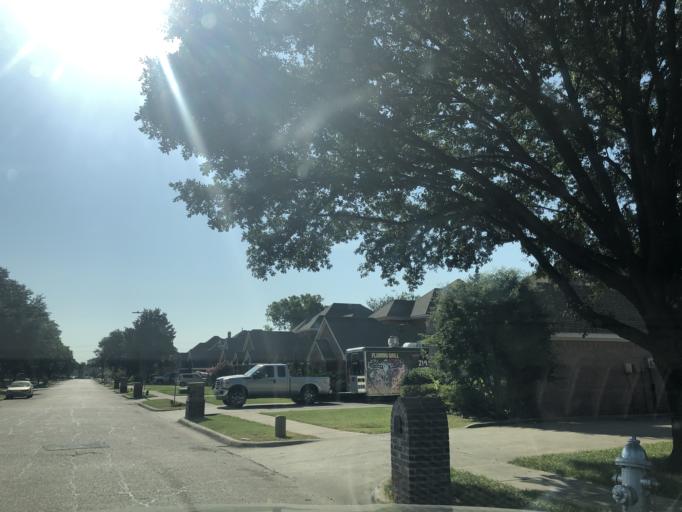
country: US
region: Texas
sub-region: Dallas County
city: Garland
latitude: 32.8643
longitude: -96.6430
